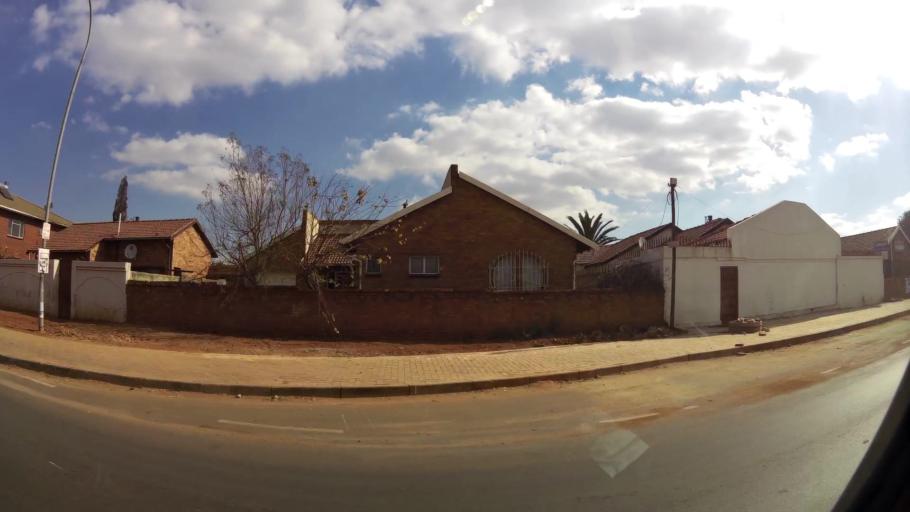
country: ZA
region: Gauteng
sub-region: Ekurhuleni Metropolitan Municipality
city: Tembisa
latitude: -25.9902
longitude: 28.2444
